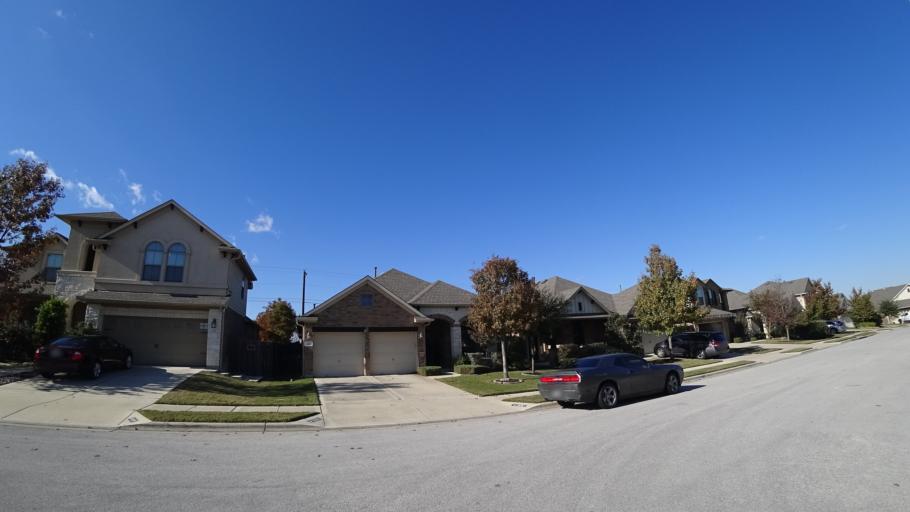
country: US
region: Texas
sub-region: Williamson County
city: Brushy Creek
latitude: 30.4913
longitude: -97.7245
